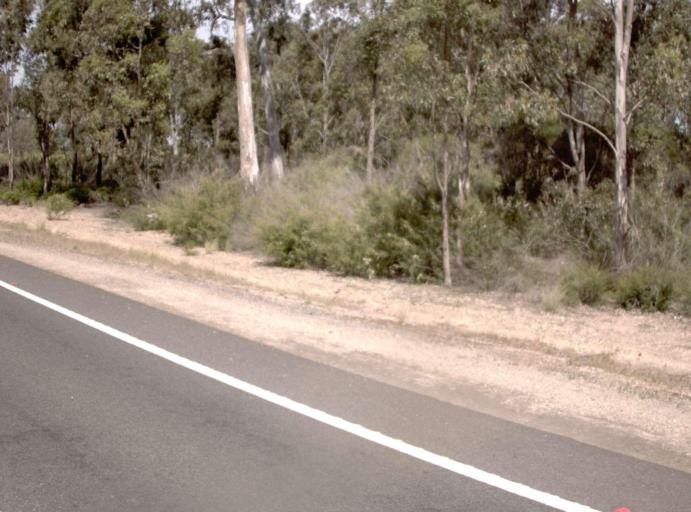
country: AU
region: Victoria
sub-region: Wellington
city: Sale
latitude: -37.9134
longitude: 147.3044
